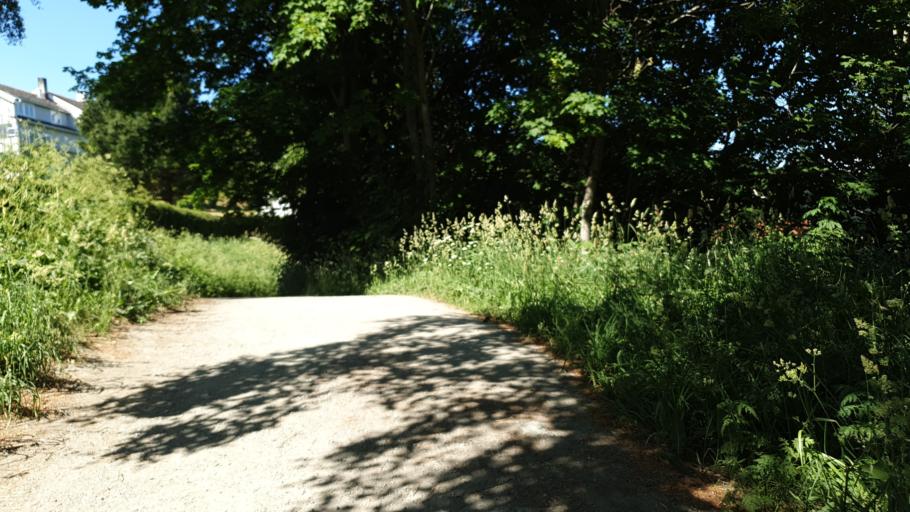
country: NO
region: Sor-Trondelag
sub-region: Trondheim
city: Trondheim
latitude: 63.4486
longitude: 10.4659
